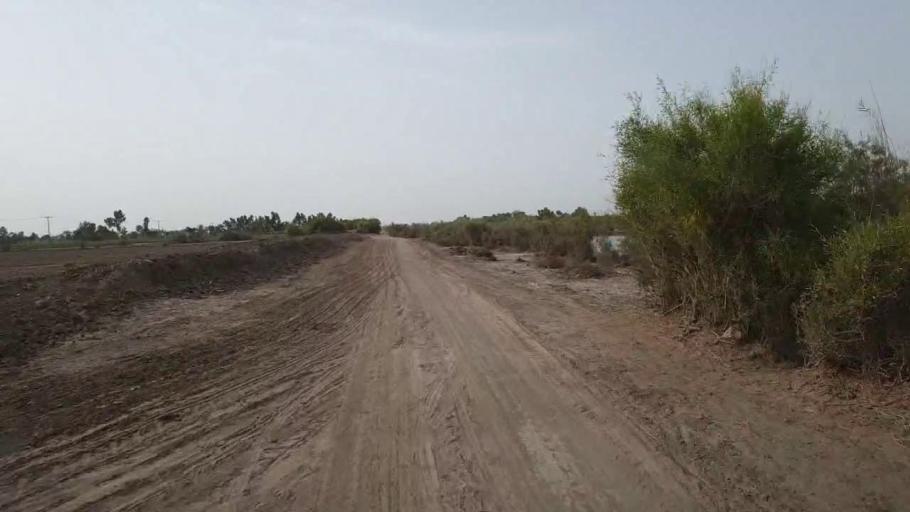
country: PK
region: Sindh
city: Daur
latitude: 26.4213
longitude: 68.1592
